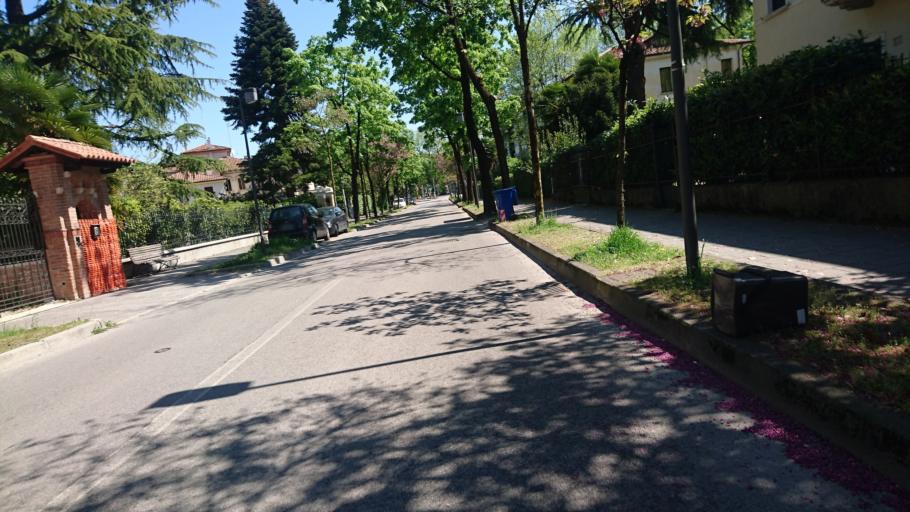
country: IT
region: Veneto
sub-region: Provincia di Treviso
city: Treviso
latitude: 45.6633
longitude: 12.2344
